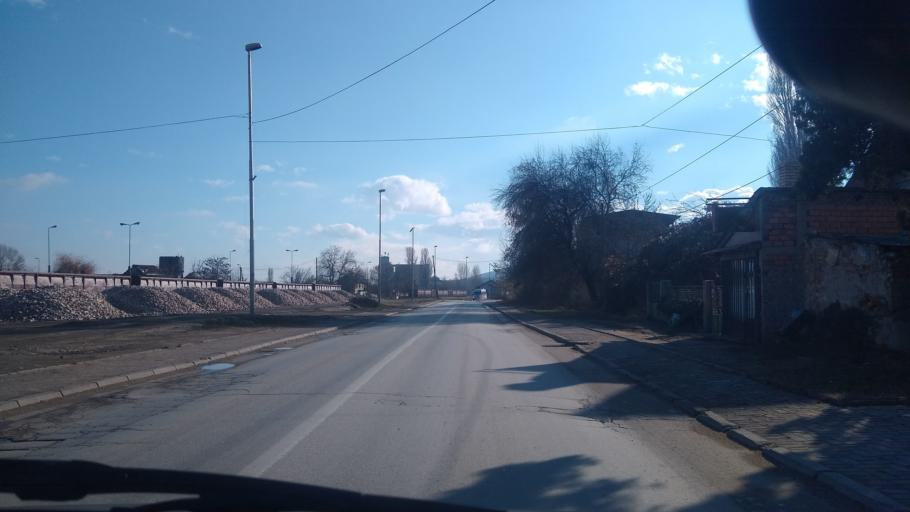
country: MK
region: Bitola
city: Bitola
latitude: 41.0232
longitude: 21.3420
